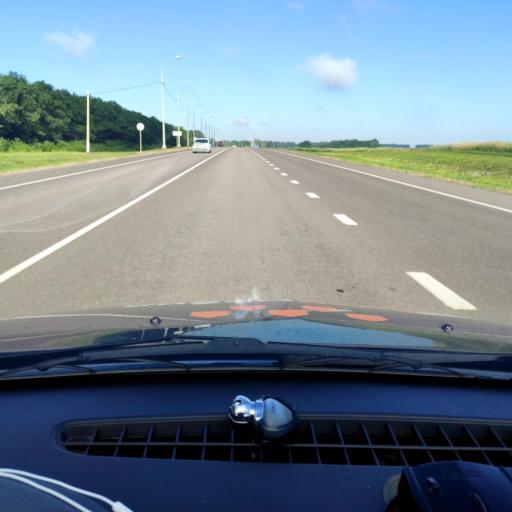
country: RU
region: Orjol
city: Pokrovskoye
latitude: 52.6213
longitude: 36.8552
